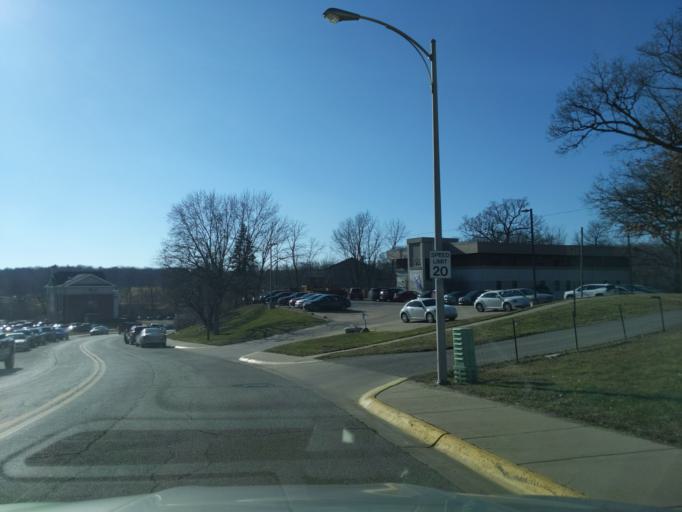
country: US
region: Indiana
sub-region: Tippecanoe County
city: West Lafayette
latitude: 40.4335
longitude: -86.9248
